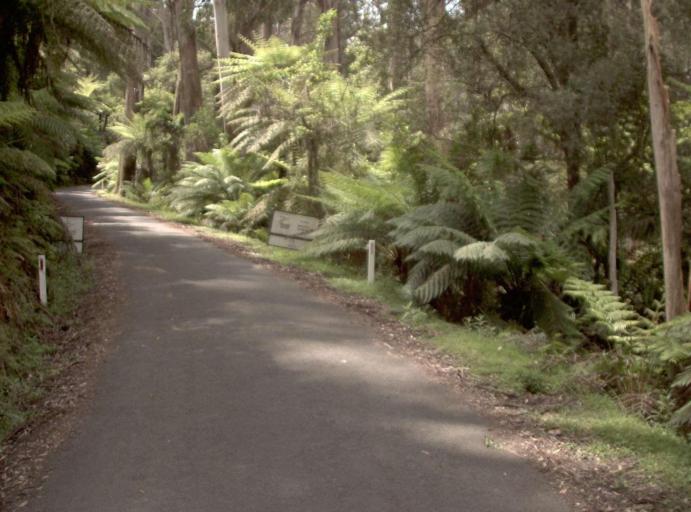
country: AU
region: Victoria
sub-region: Latrobe
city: Traralgon
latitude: -38.4435
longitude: 146.5365
